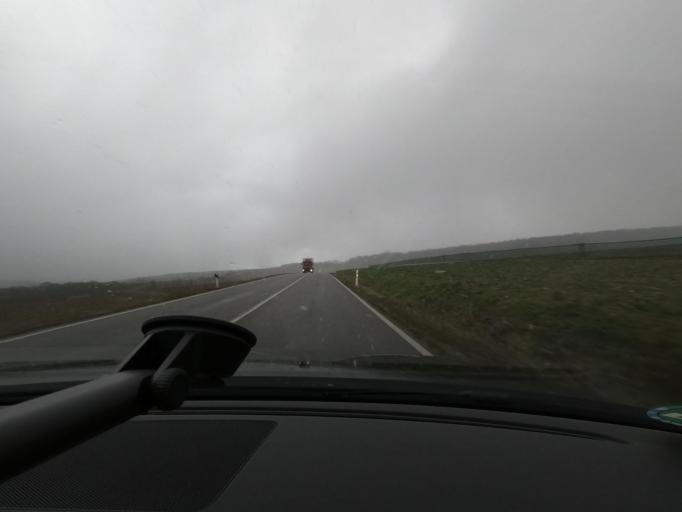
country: DE
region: Thuringia
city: Helmsdorf
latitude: 51.2888
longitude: 10.3509
